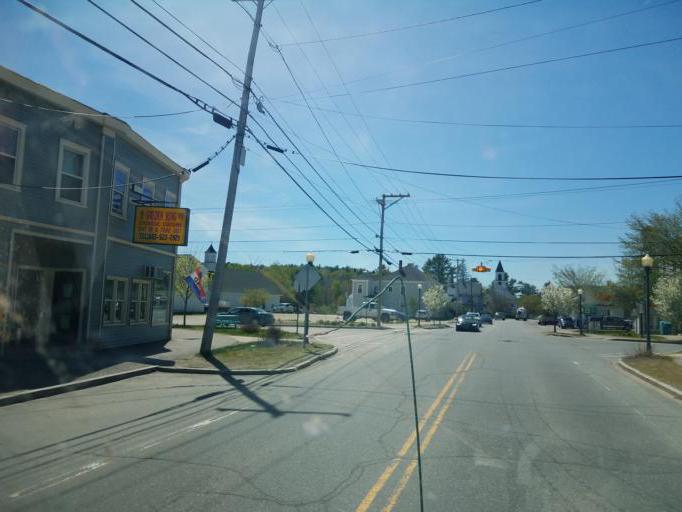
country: US
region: New Hampshire
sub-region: Grafton County
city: Grafton
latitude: 43.6465
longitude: -72.0113
